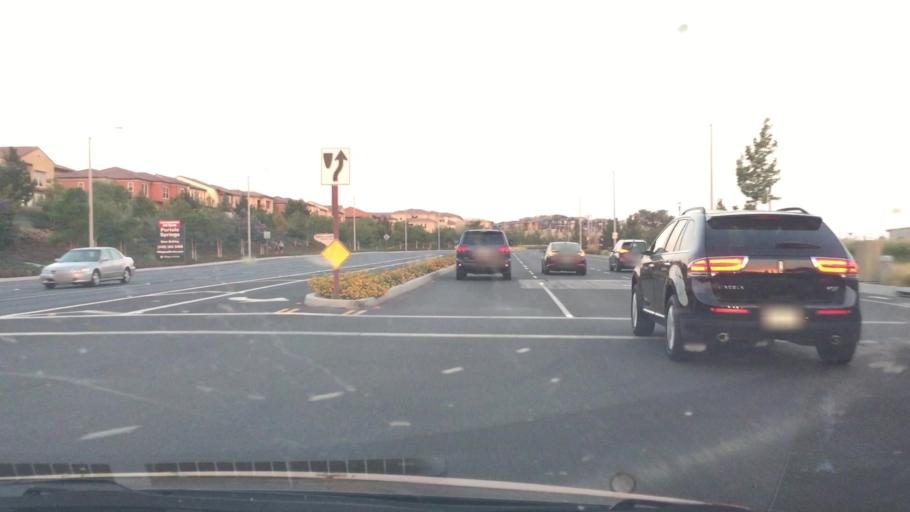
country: US
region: California
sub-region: Orange County
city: Lake Forest
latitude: 33.6852
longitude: -117.7191
